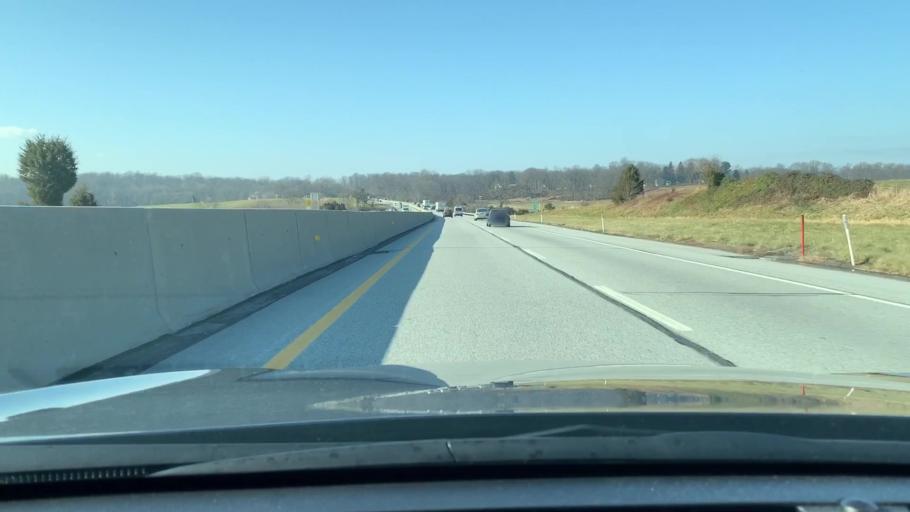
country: US
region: Pennsylvania
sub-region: Lancaster County
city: Elizabethtown
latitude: 40.2084
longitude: -76.6087
